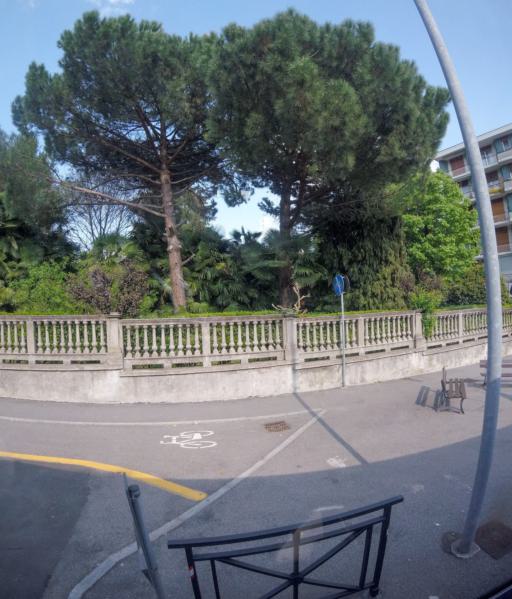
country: IT
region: Piedmont
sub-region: Provincia di Novara
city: Arona
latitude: 45.7582
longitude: 8.5553
